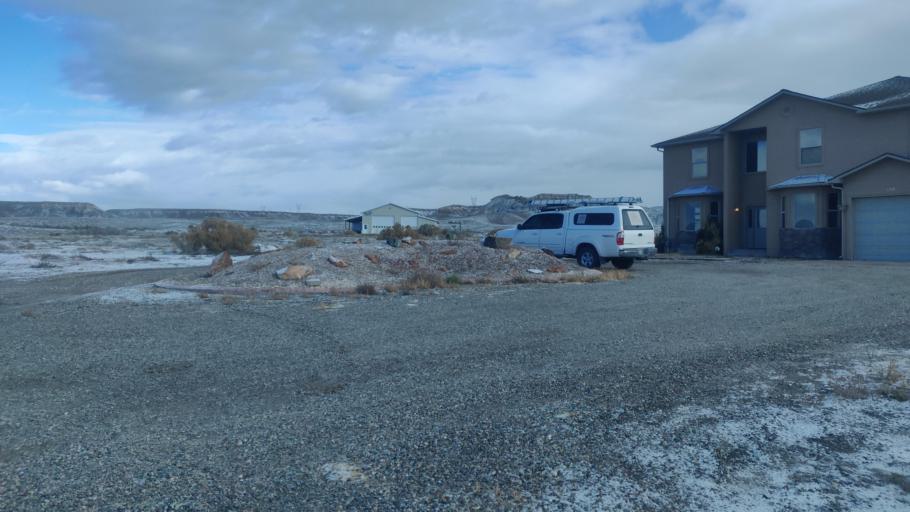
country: US
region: Colorado
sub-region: Mesa County
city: Clifton
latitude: 39.0026
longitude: -108.4245
